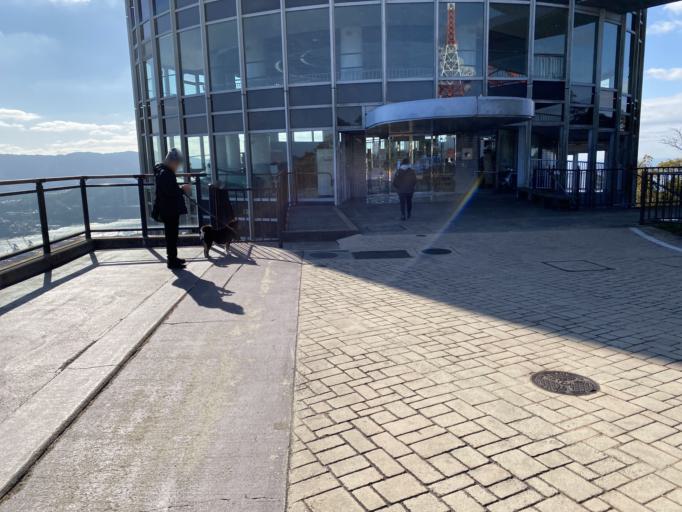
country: JP
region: Nagasaki
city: Nagasaki-shi
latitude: 32.7529
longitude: 129.8496
